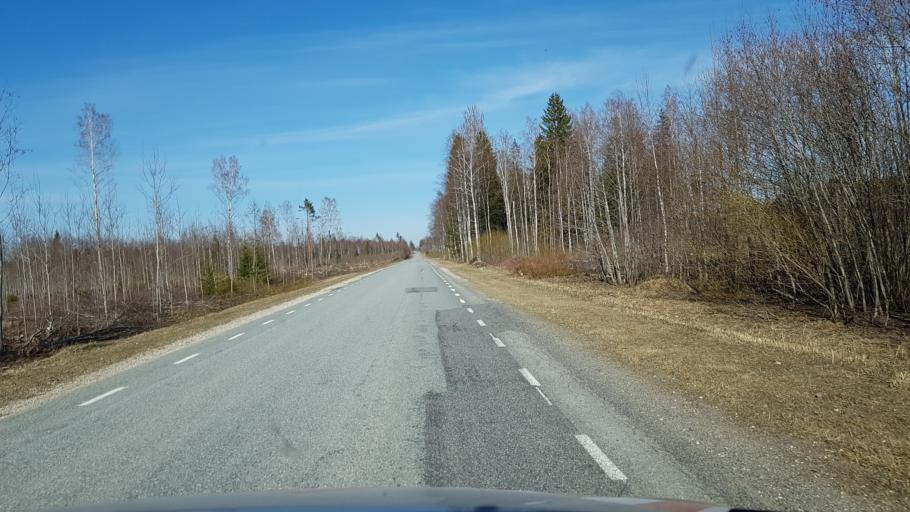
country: EE
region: Laeaene-Virumaa
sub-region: Rakke vald
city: Rakke
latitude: 59.0103
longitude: 26.3347
